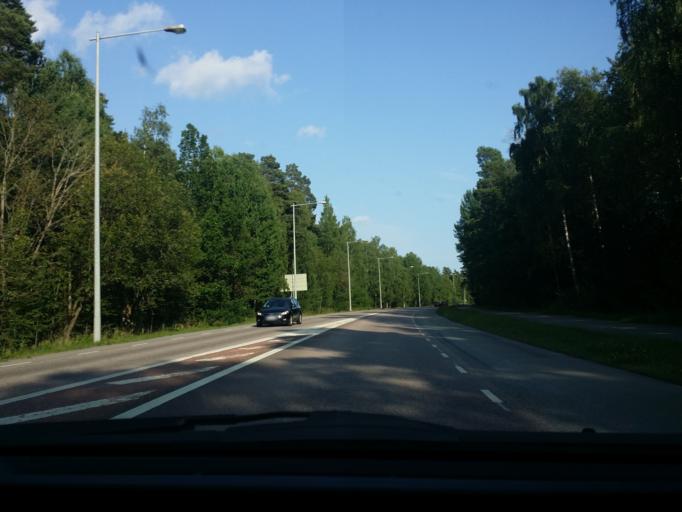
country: SE
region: Vaestmanland
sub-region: Vasteras
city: Hokasen
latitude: 59.6310
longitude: 16.5889
